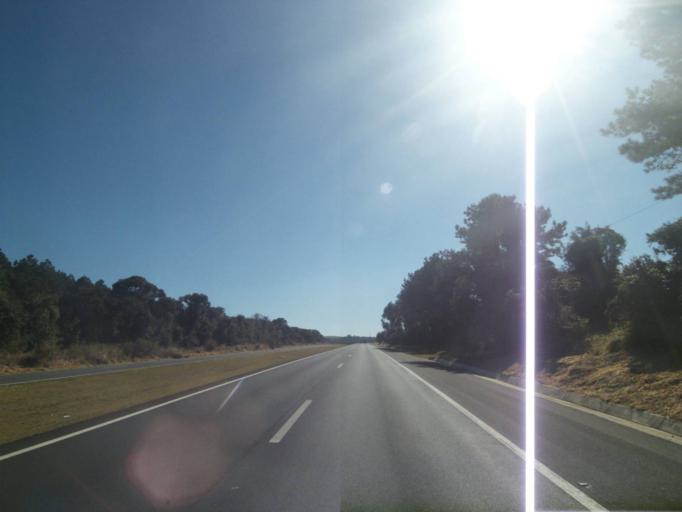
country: BR
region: Parana
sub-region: Carambei
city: Carambei
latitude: -24.8843
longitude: -50.4376
